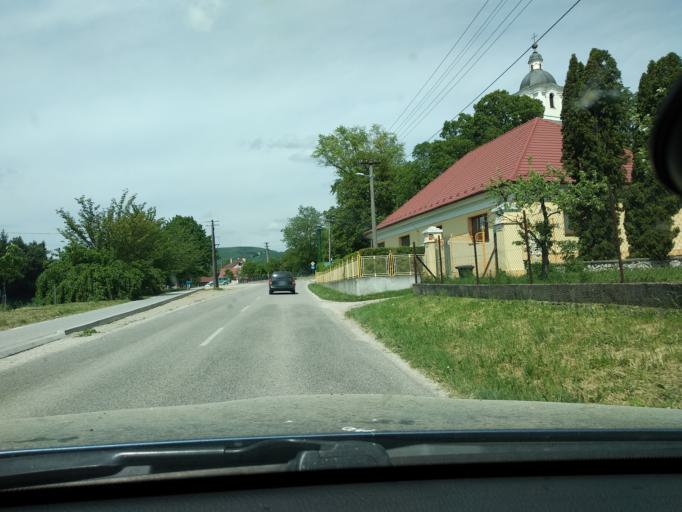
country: SK
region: Trenciansky
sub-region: Okres Nove Mesto nad Vahom
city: Nove Mesto nad Vahom
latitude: 48.8229
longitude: 17.8437
